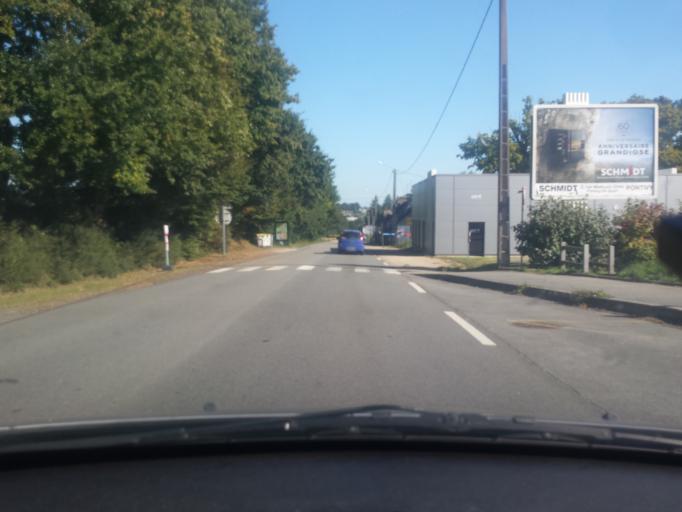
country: FR
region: Brittany
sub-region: Departement du Morbihan
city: Pontivy
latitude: 48.0589
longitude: -2.9525
